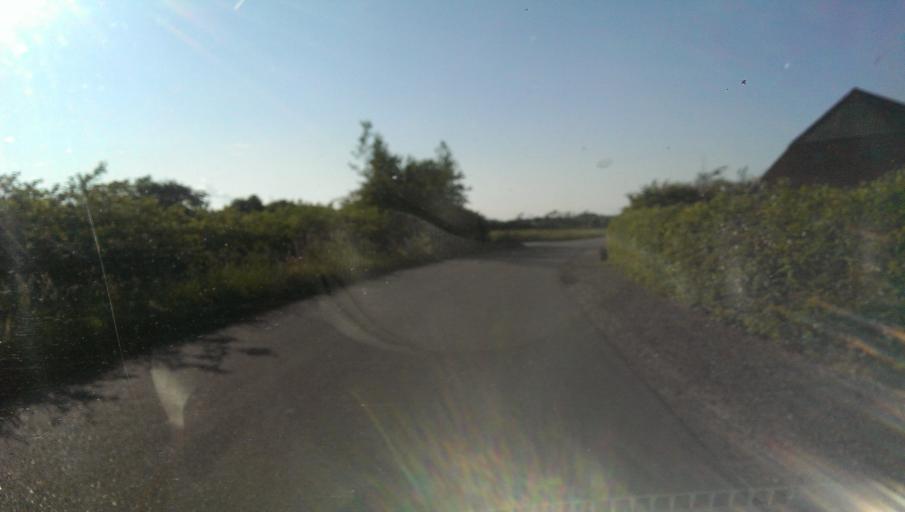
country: DK
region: South Denmark
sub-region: Esbjerg Kommune
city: Bramming
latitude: 55.5575
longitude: 8.6982
